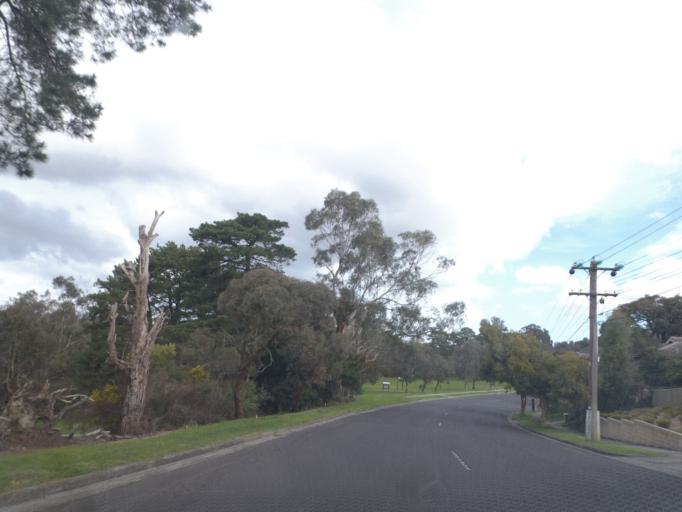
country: AU
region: Victoria
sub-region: Knox
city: Wantirna
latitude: -37.8387
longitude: 145.2134
